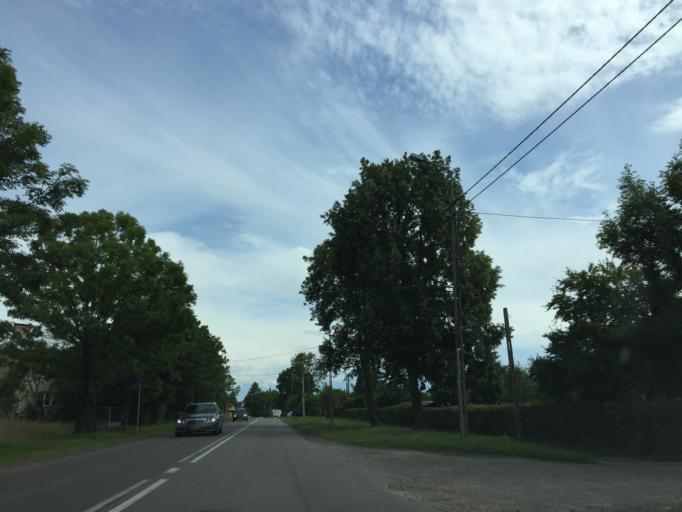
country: PL
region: Podlasie
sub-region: Powiat siemiatycki
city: Siemiatycze
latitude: 52.4351
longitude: 22.8575
